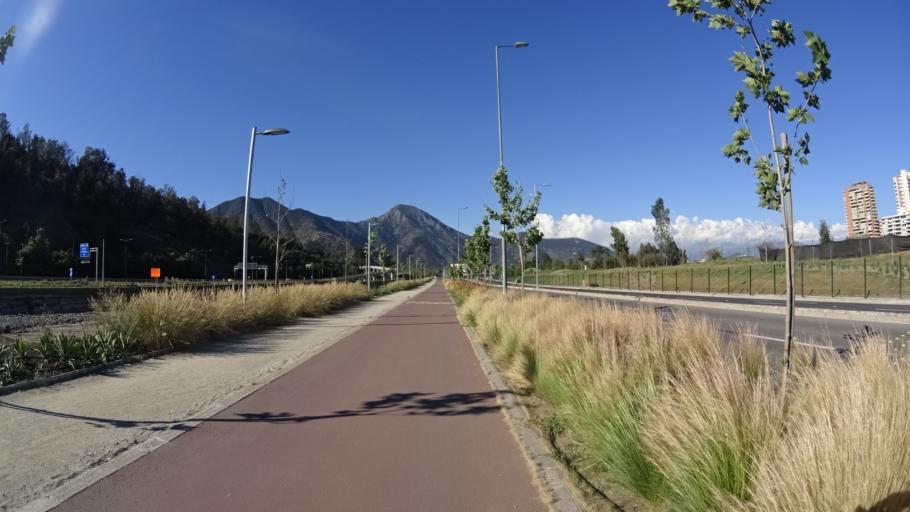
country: CL
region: Santiago Metropolitan
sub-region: Provincia de Santiago
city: Villa Presidente Frei, Nunoa, Santiago, Chile
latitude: -33.3951
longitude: -70.6027
